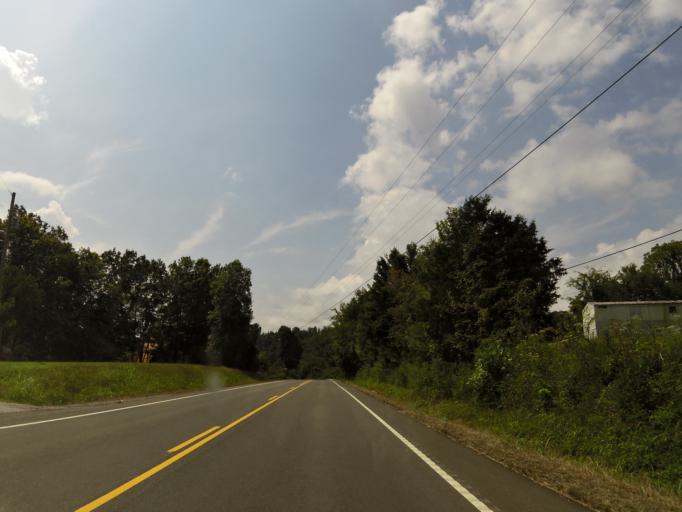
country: US
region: Tennessee
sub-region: Perry County
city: Linden
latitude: 35.7136
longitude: -87.7973
